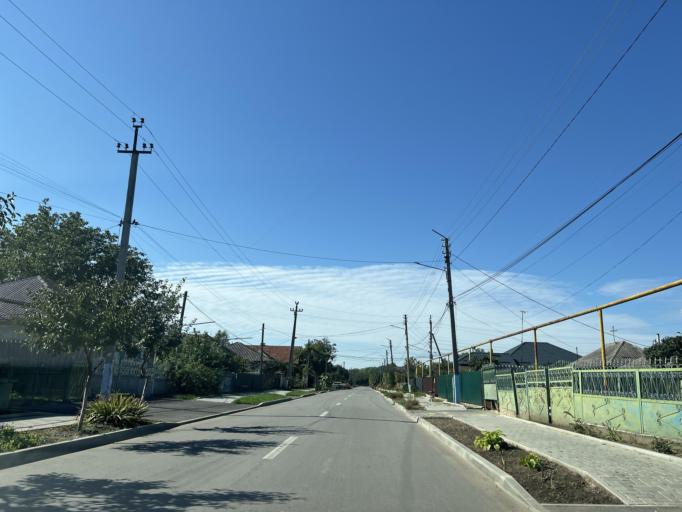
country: RO
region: Iasi
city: Ungheni-Prut
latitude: 47.1945
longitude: 27.7962
